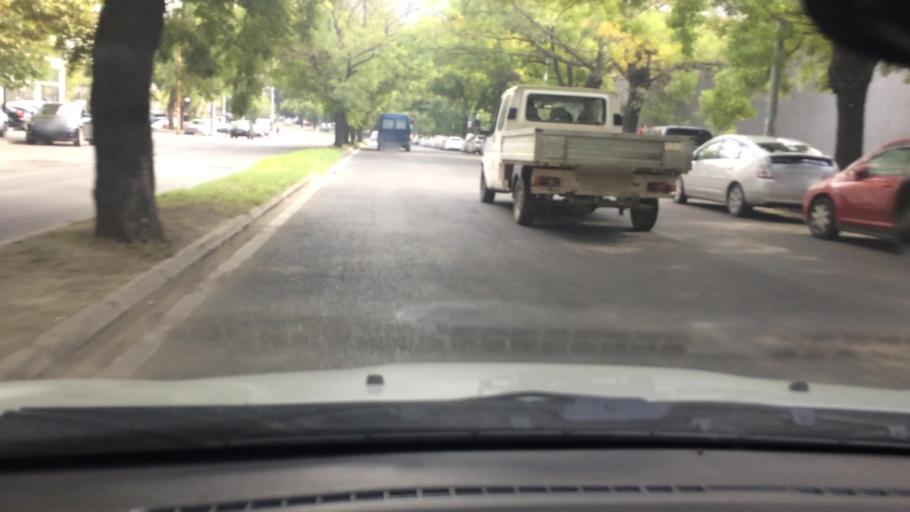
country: GE
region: T'bilisi
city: Tbilisi
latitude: 41.6746
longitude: 44.8304
